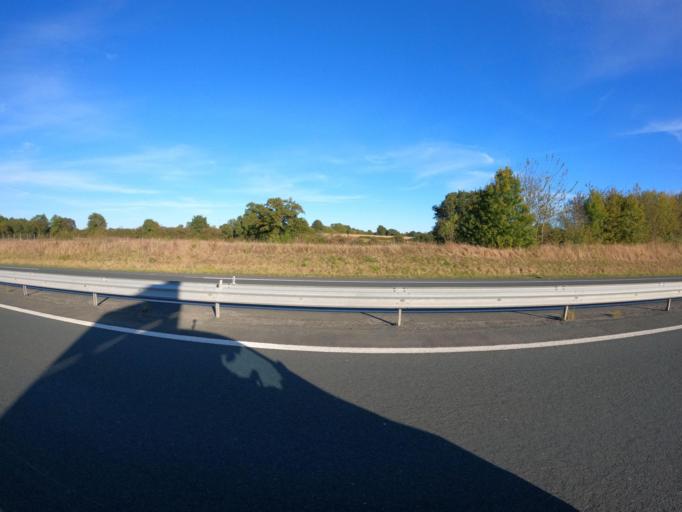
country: FR
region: Pays de la Loire
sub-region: Departement de Maine-et-Loire
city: Mazieres-en-Mauges
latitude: 47.0774
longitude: -0.8259
